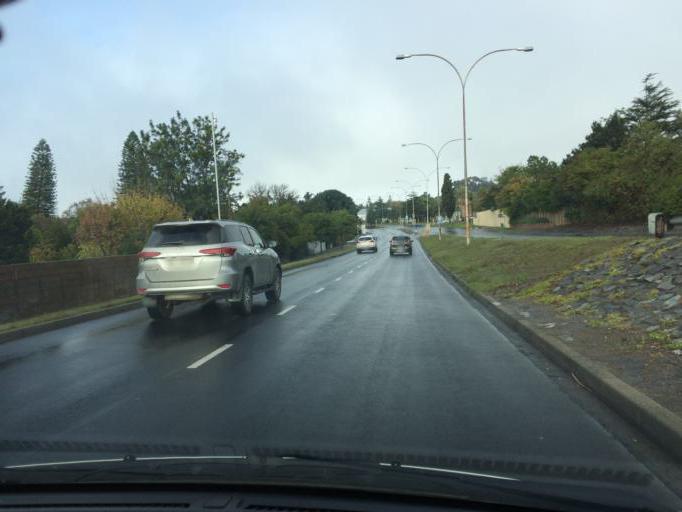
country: ZA
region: Western Cape
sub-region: City of Cape Town
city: Kraaifontein
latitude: -33.8437
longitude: 18.6463
